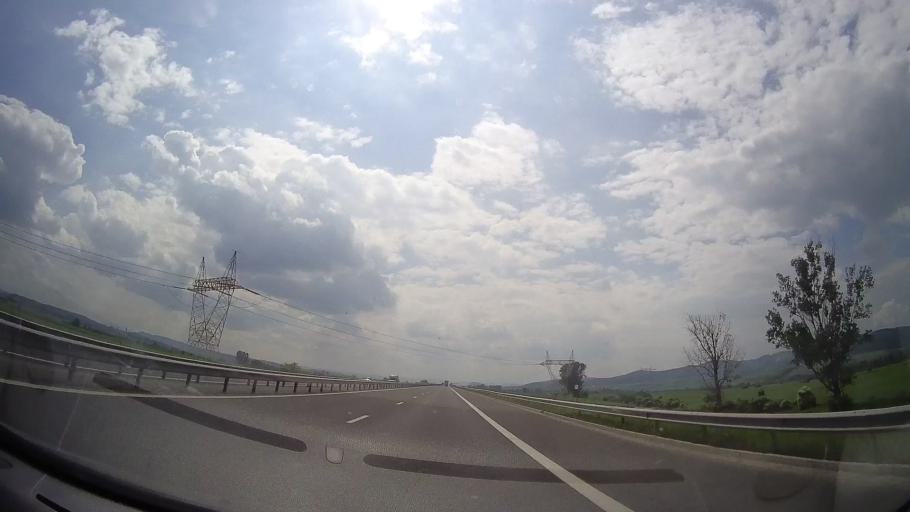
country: RO
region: Hunedoara
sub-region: Comuna Geoagiu
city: Geoagiu
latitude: 45.8812
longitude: 23.2132
